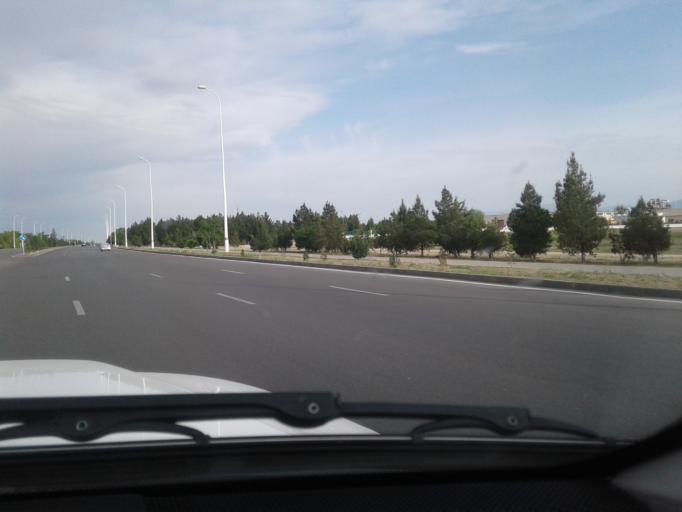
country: TM
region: Ahal
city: Abadan
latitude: 38.0085
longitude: 58.2822
